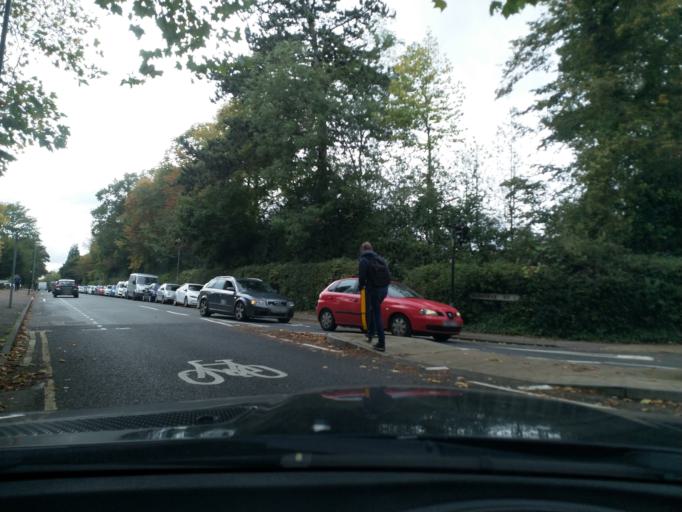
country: GB
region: England
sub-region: City and Borough of Birmingham
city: Birmingham
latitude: 52.4577
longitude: -1.9296
